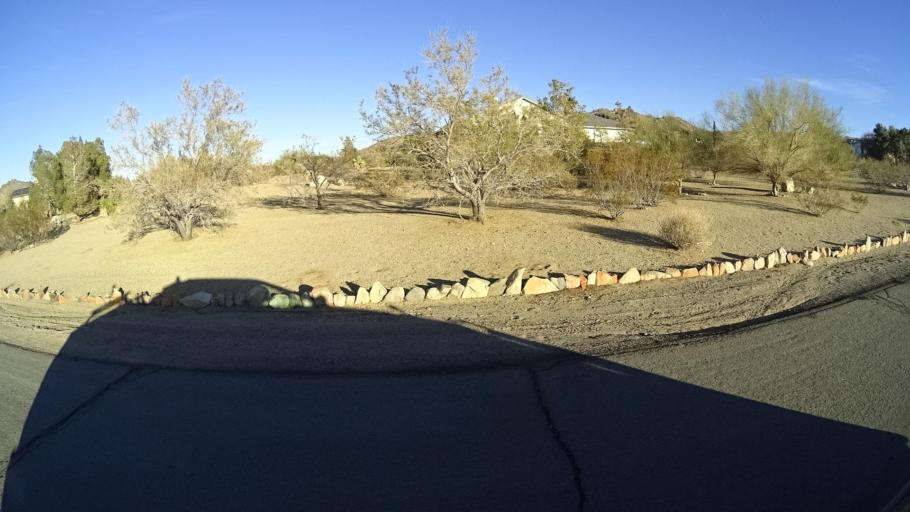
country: US
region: California
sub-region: Kern County
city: Ridgecrest
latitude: 35.5774
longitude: -117.6523
